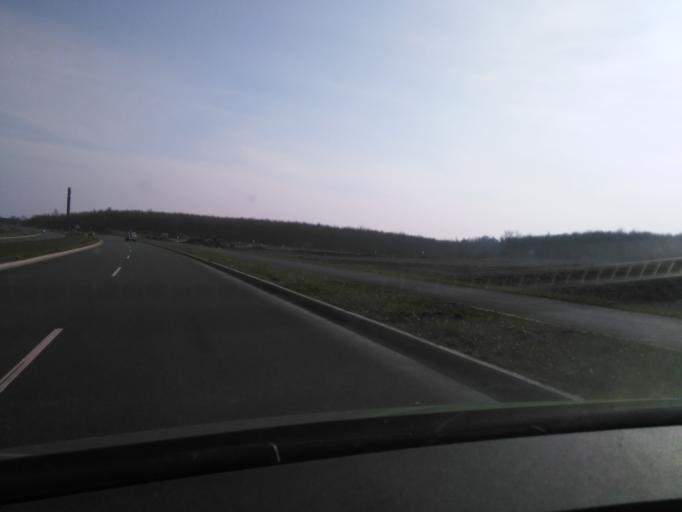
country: DK
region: Central Jutland
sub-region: Arhus Kommune
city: Arhus
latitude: 56.1877
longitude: 10.1624
